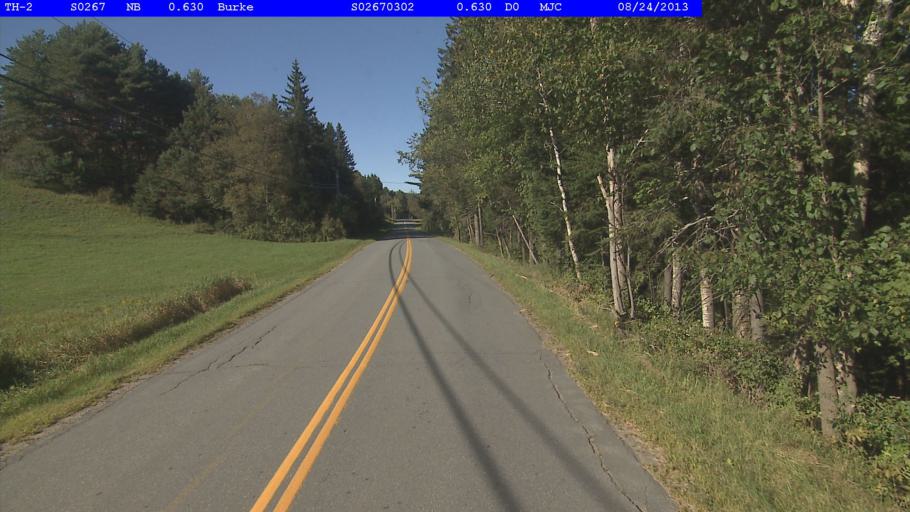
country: US
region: Vermont
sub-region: Caledonia County
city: Lyndonville
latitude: 44.5958
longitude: -71.9428
